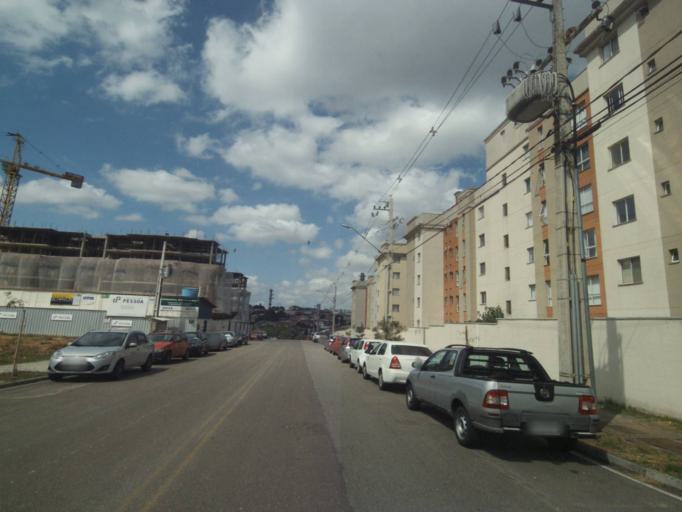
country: BR
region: Parana
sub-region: Curitiba
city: Curitiba
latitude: -25.5025
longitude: -49.3096
